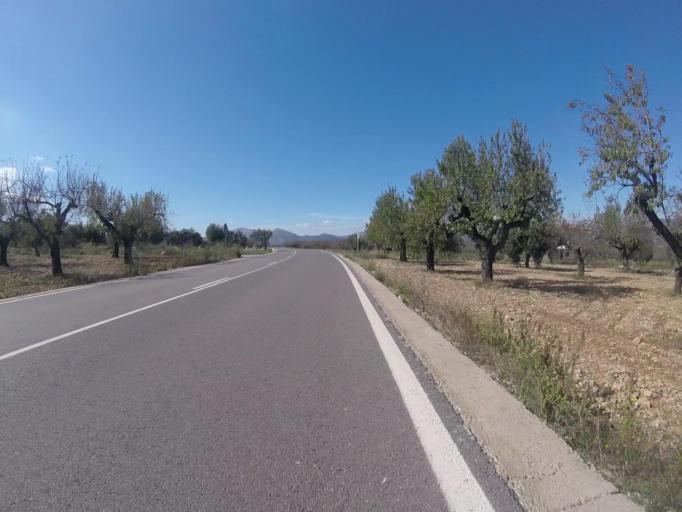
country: ES
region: Valencia
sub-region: Provincia de Castello
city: Albocasser
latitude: 40.3492
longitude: 0.0027
